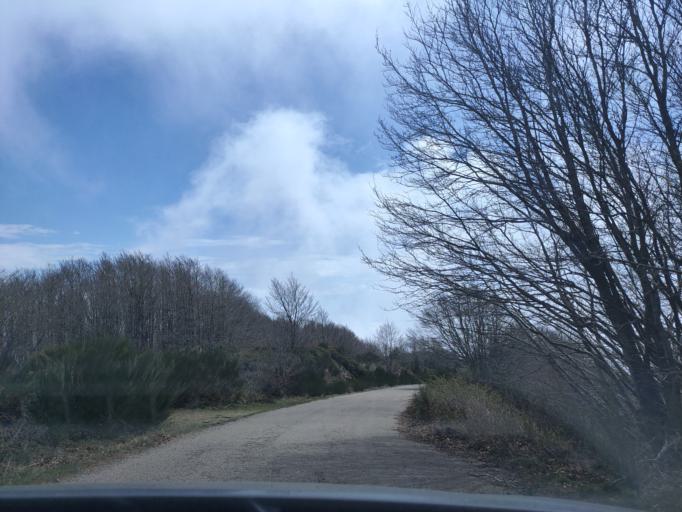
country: ES
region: Catalonia
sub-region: Provincia de Barcelona
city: Fogars de Montclus
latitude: 41.7655
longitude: 2.4548
